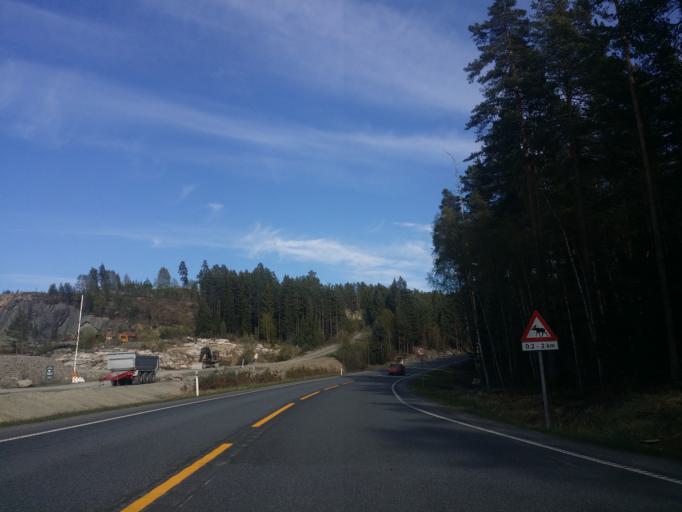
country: NO
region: Telemark
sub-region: Notodden
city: Notodden
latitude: 59.5844
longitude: 9.3081
